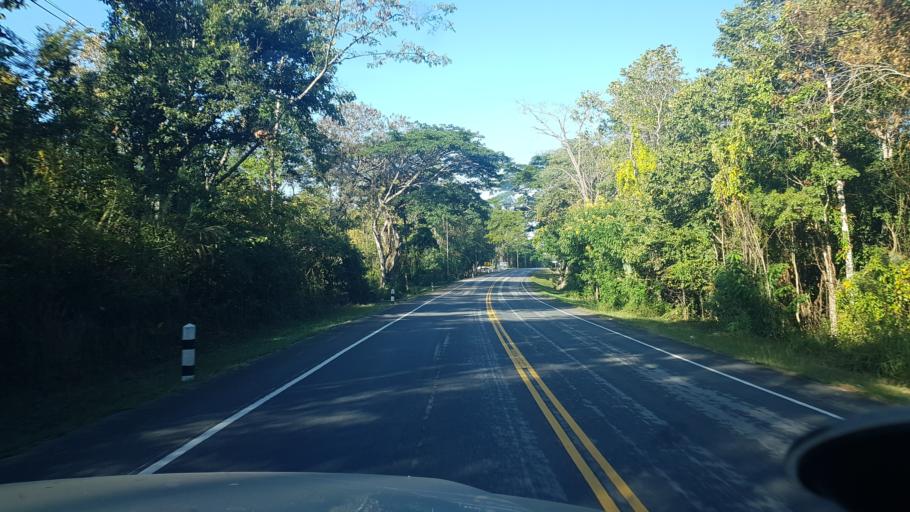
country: TH
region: Phetchabun
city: Lom Sak
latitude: 16.7360
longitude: 101.4351
